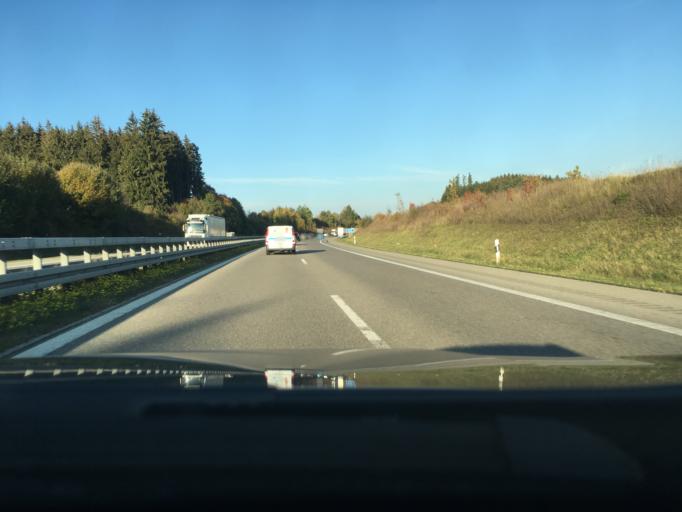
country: DE
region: Baden-Wuerttemberg
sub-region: Tuebingen Region
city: Leutkirch im Allgau
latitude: 47.7939
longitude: 9.9688
